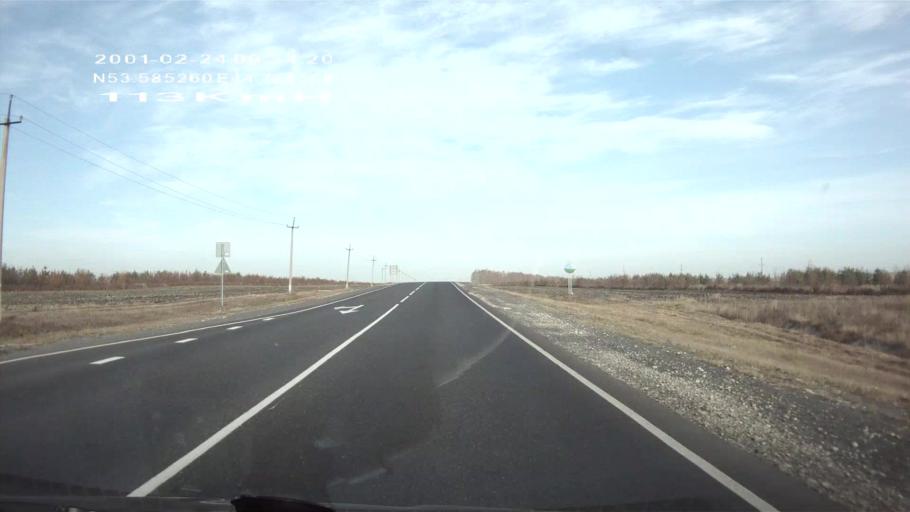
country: RU
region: Penza
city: Mokshan
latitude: 53.5866
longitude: 44.7284
